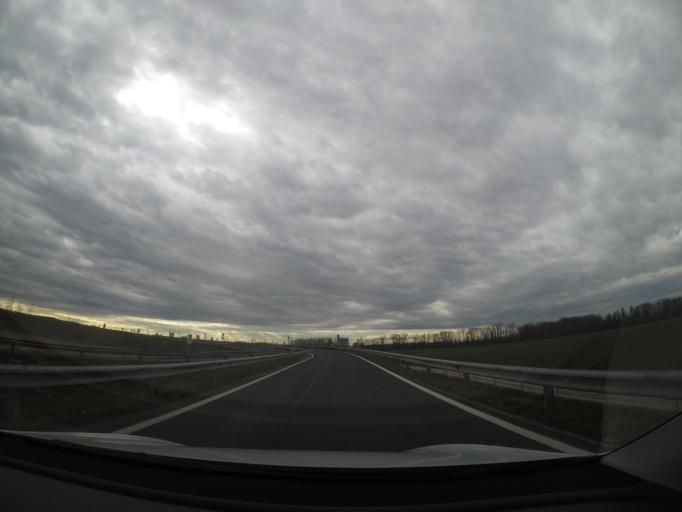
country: AT
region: Lower Austria
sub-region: Politischer Bezirk Baden
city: Ebreichsdorf
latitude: 47.9287
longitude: 16.3896
